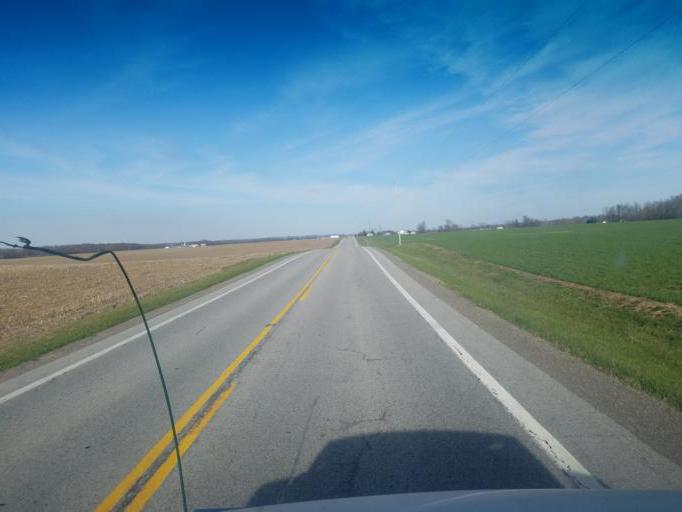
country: US
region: Ohio
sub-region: Logan County
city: De Graff
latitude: 40.3383
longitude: -83.9748
